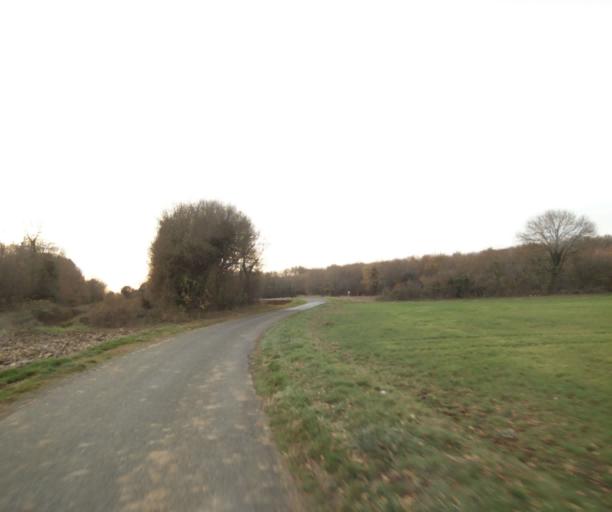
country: FR
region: Poitou-Charentes
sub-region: Departement de la Charente-Maritime
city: Fontcouverte
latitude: 45.8162
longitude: -0.5925
